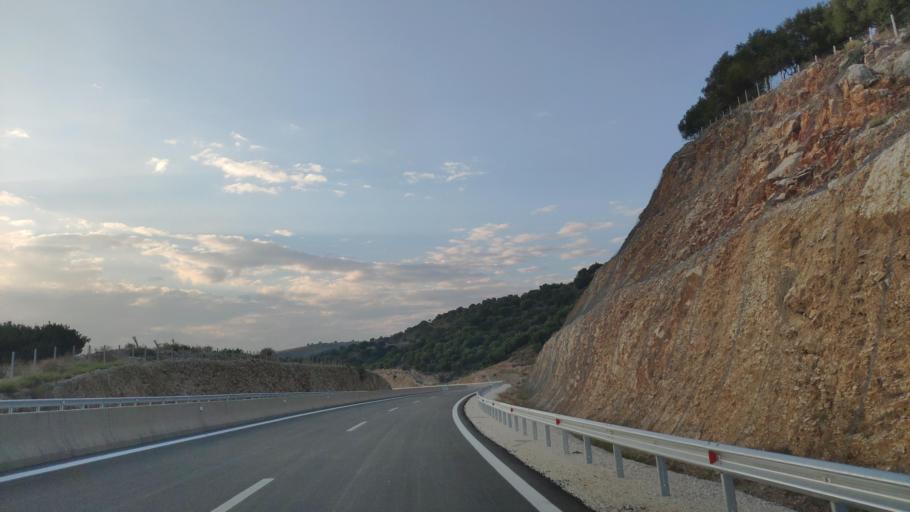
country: GR
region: West Greece
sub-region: Nomos Aitolias kai Akarnanias
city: Katouna
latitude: 38.8334
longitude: 21.1168
